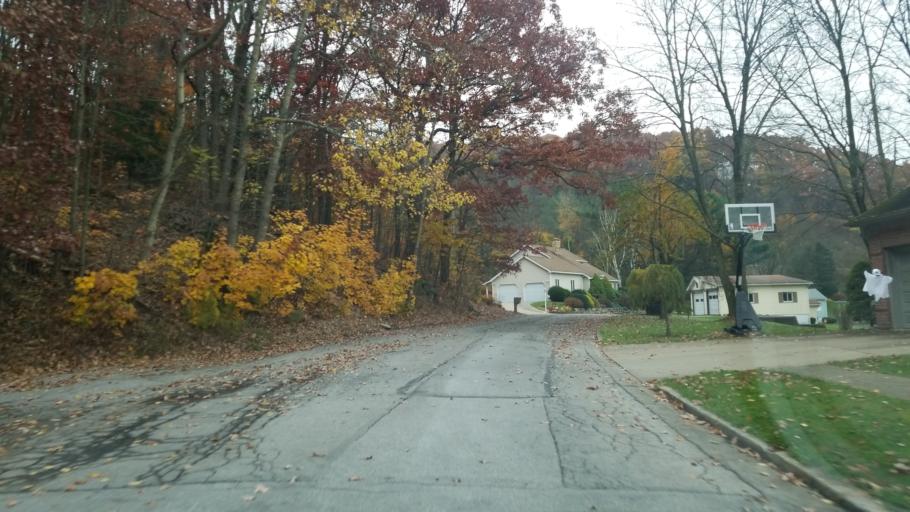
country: US
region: Pennsylvania
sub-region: Clearfield County
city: Clearfield
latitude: 41.0124
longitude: -78.4322
